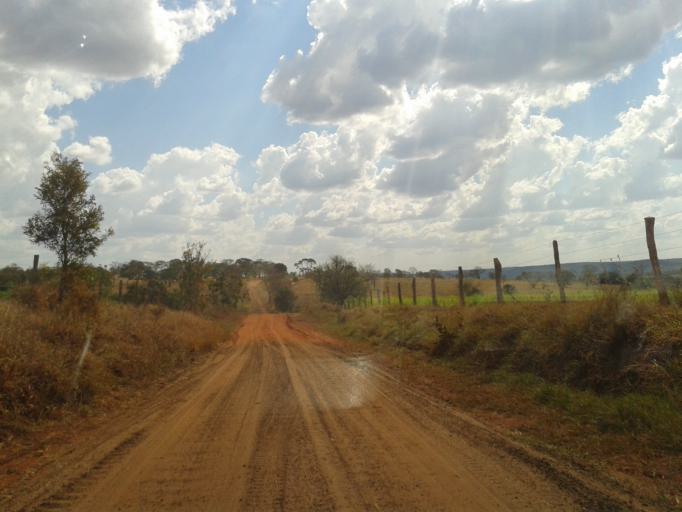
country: BR
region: Minas Gerais
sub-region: Santa Vitoria
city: Santa Vitoria
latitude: -19.2023
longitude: -49.9002
